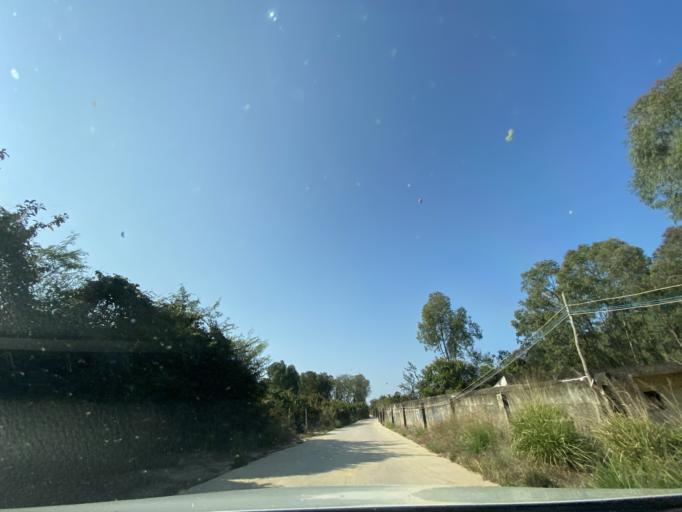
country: CN
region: Hainan
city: Haitangwan
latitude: 18.3984
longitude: 109.7683
